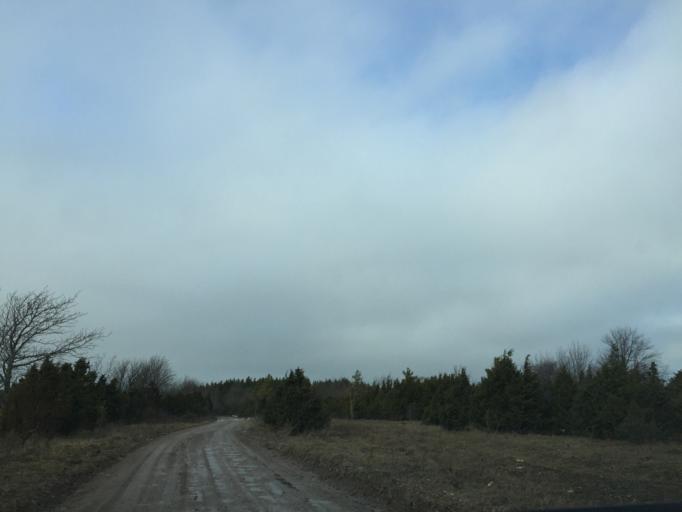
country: EE
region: Saare
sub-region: Kuressaare linn
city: Kuressaare
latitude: 58.4943
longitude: 21.9322
